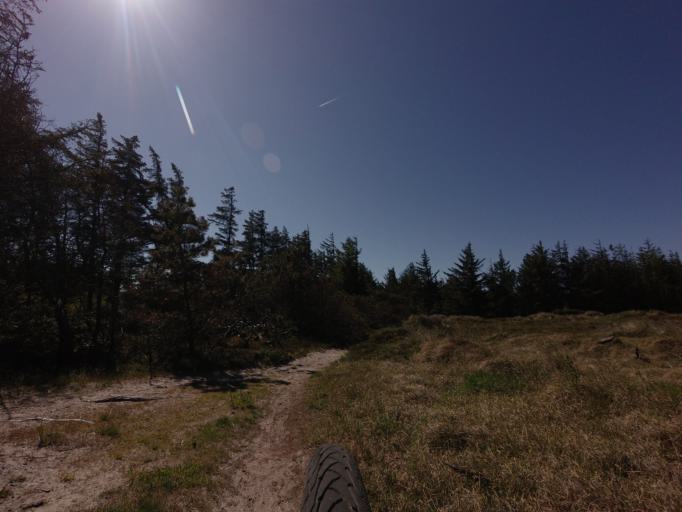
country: DK
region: North Denmark
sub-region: Jammerbugt Kommune
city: Pandrup
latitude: 57.2934
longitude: 9.6460
